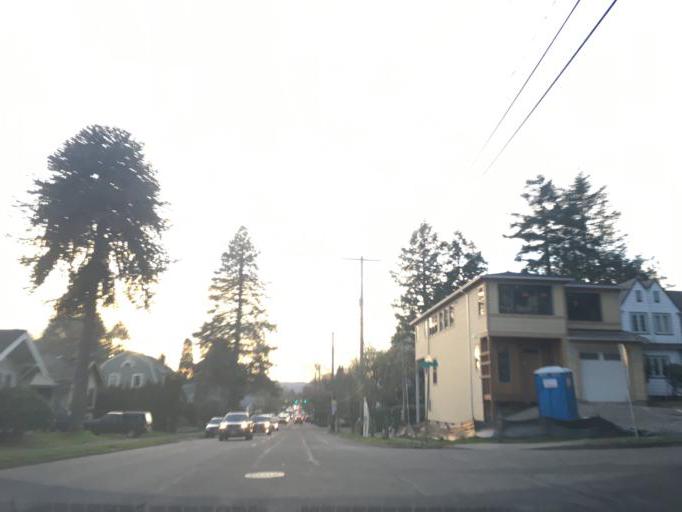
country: US
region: Oregon
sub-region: Multnomah County
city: Portland
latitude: 45.5482
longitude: -122.6346
